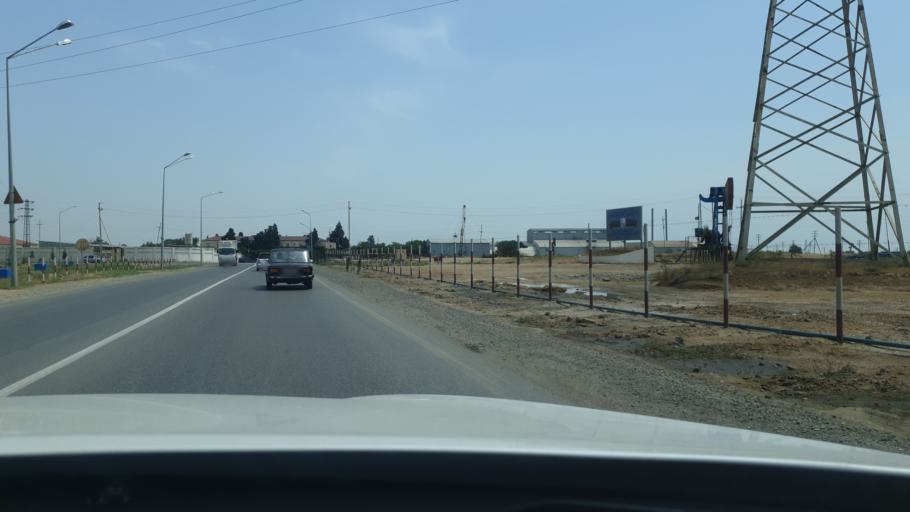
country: AZ
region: Baki
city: Qaracuxur
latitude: 40.3951
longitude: 49.9947
